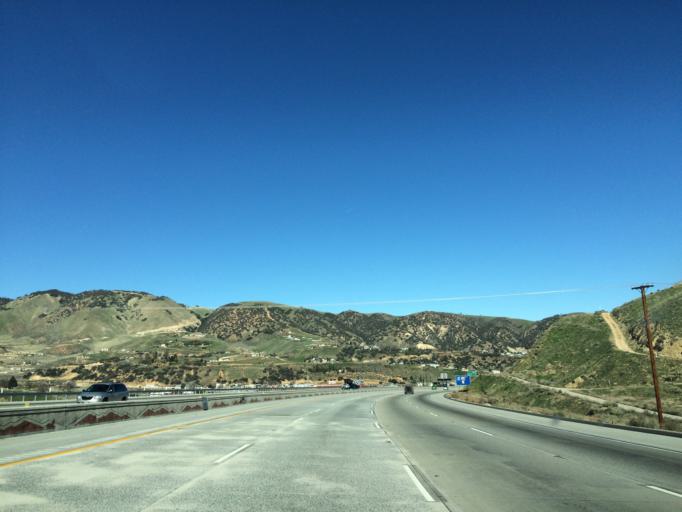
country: US
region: California
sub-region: Kern County
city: Lebec
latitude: 34.8091
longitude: -118.8837
